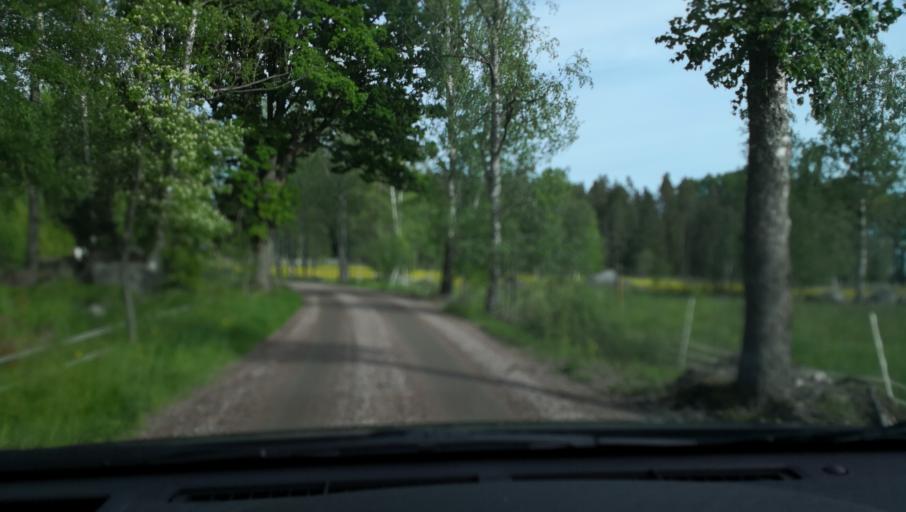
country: SE
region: Vaestmanland
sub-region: Kungsors Kommun
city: Kungsoer
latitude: 59.3607
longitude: 16.0256
